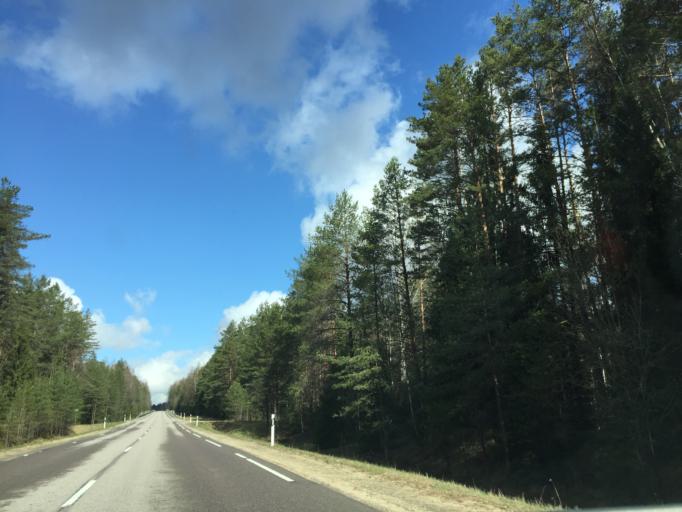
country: LV
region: Apes Novads
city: Ape
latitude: 57.5166
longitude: 26.7679
